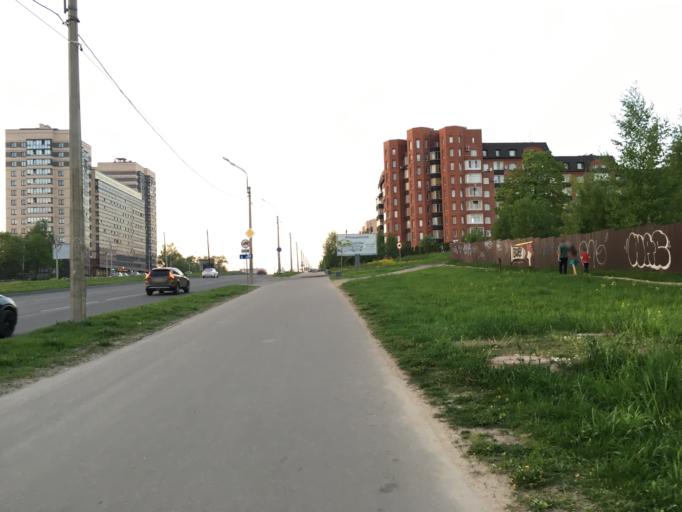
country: RU
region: St.-Petersburg
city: Kolomyagi
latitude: 60.0185
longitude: 30.2799
